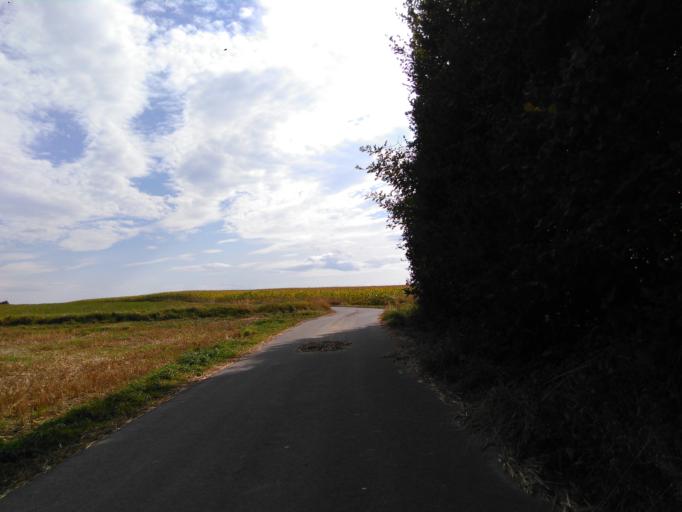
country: BE
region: Wallonia
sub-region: Province du Luxembourg
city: Gouvy
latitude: 50.1684
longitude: 5.9643
